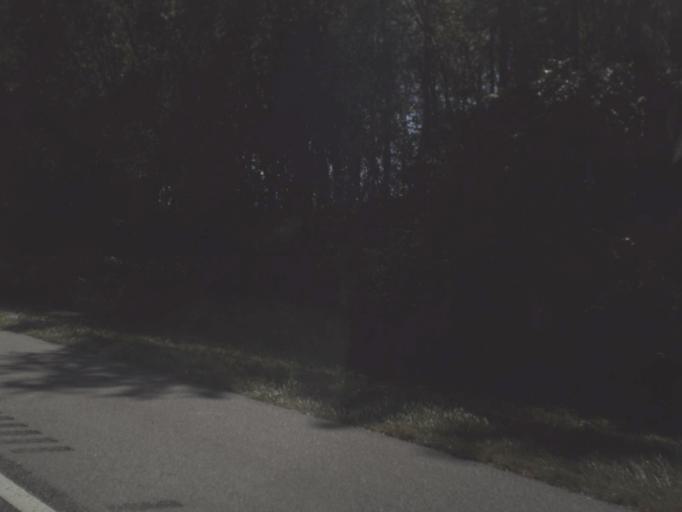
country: US
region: Florida
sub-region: Sumter County
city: Wildwood
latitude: 28.8494
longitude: -82.0824
